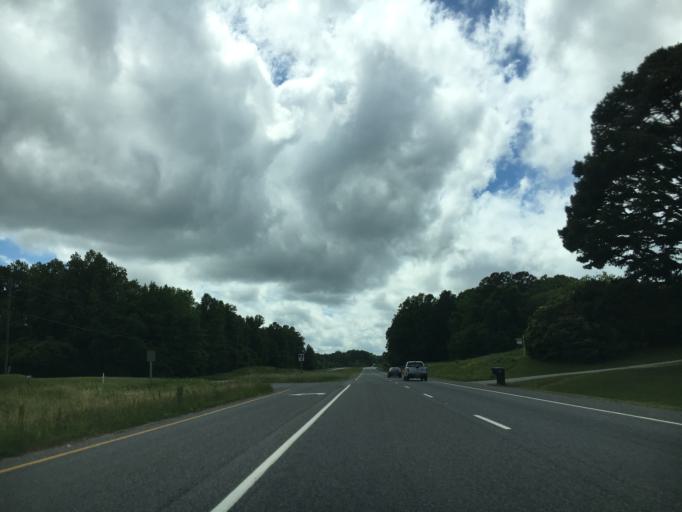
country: US
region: Virginia
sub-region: Mecklenburg County
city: Boydton
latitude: 36.6561
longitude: -78.4485
